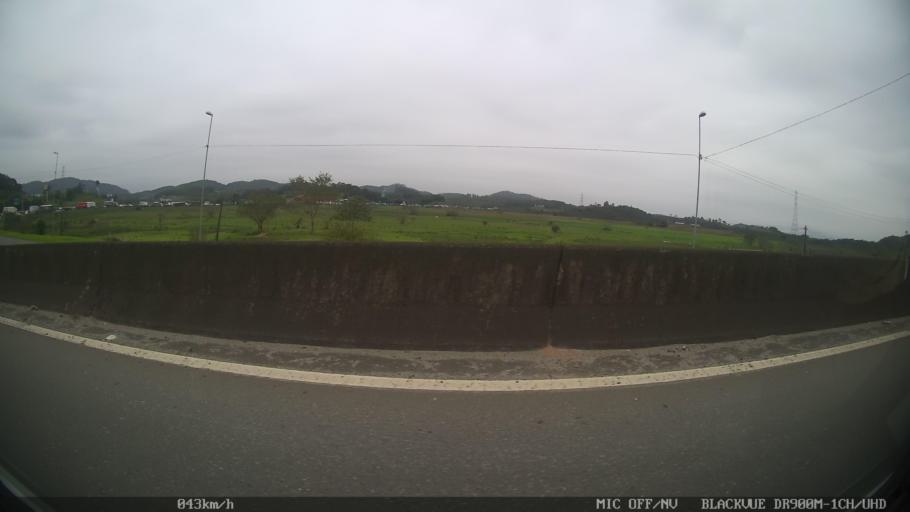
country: BR
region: Santa Catarina
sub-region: Joinville
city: Joinville
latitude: -26.3876
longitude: -48.8448
